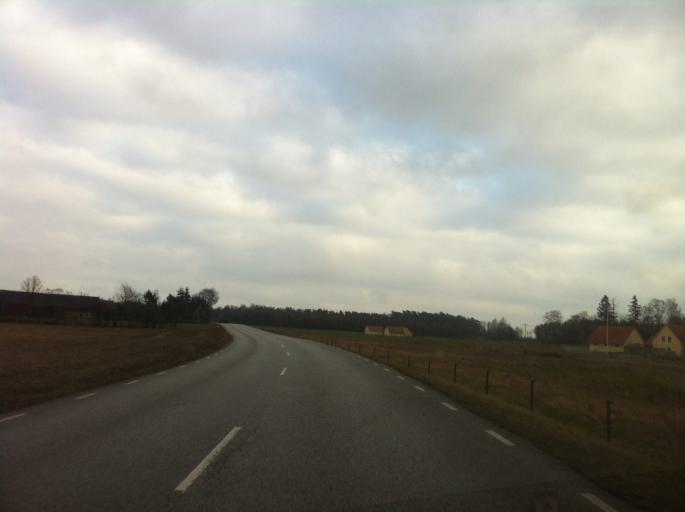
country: SE
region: Skane
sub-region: Kavlinge Kommun
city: Hofterup
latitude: 55.8225
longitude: 12.9964
